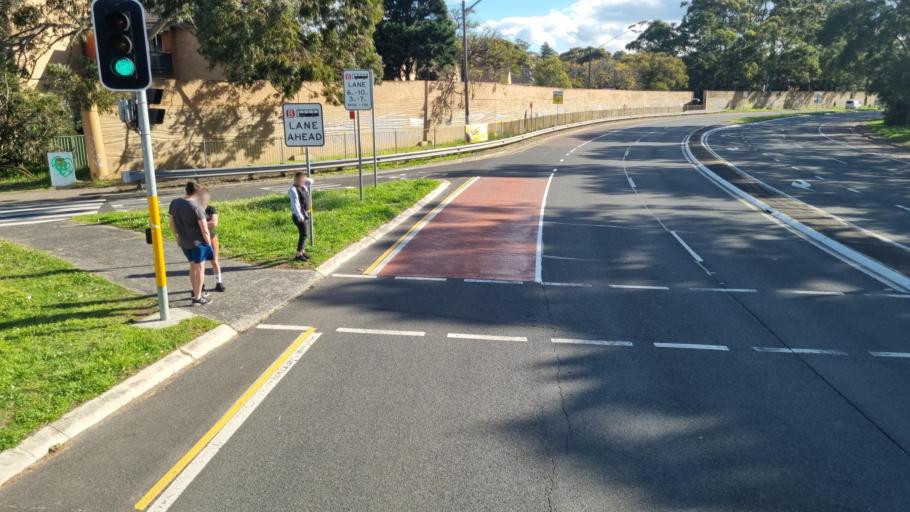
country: AU
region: New South Wales
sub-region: Manly Vale
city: Fairlight
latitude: -33.7884
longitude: 151.2658
